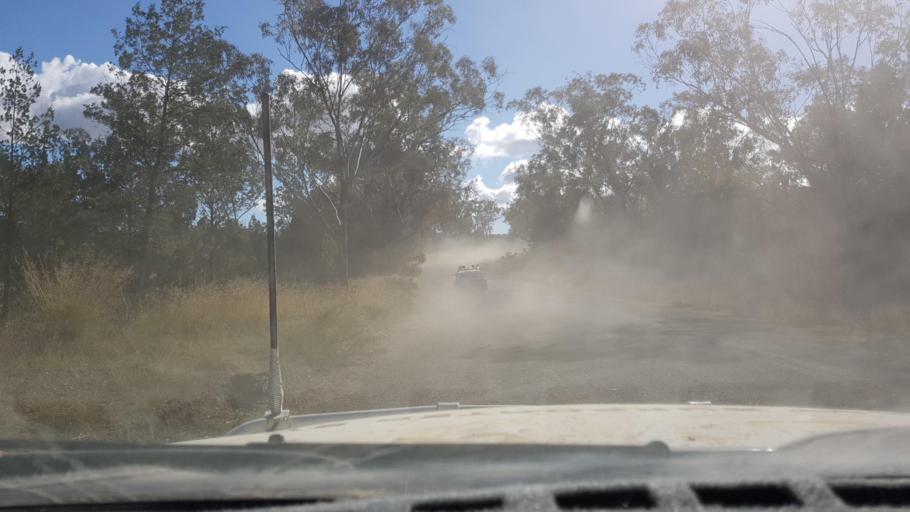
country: AU
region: New South Wales
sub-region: Tamworth Municipality
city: Manilla
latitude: -30.6486
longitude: 150.4962
